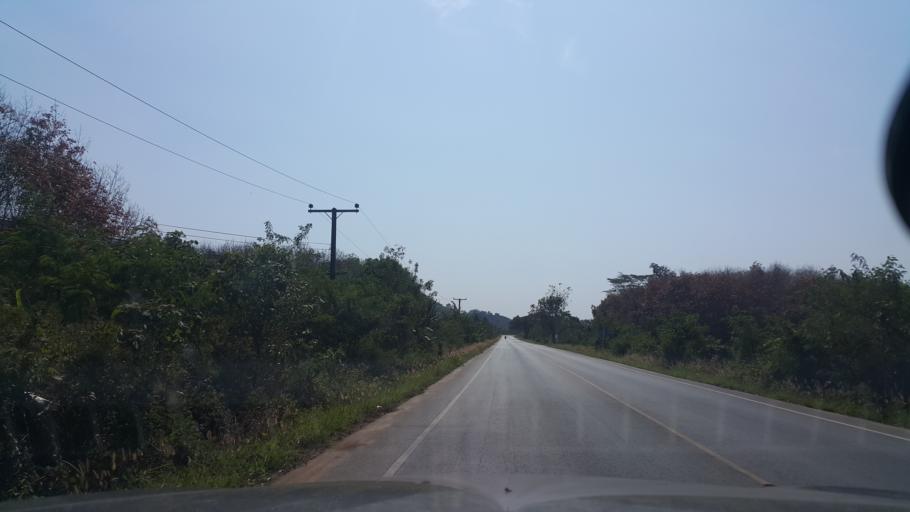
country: TH
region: Changwat Udon Thani
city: Na Yung
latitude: 17.9135
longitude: 102.0711
